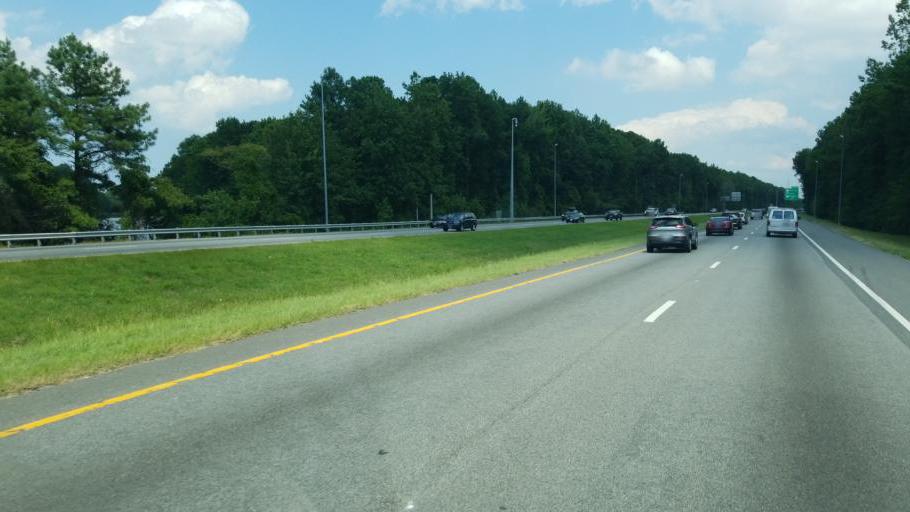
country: US
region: Virginia
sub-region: City of Portsmouth
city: Portsmouth Heights
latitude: 36.7594
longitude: -76.3287
